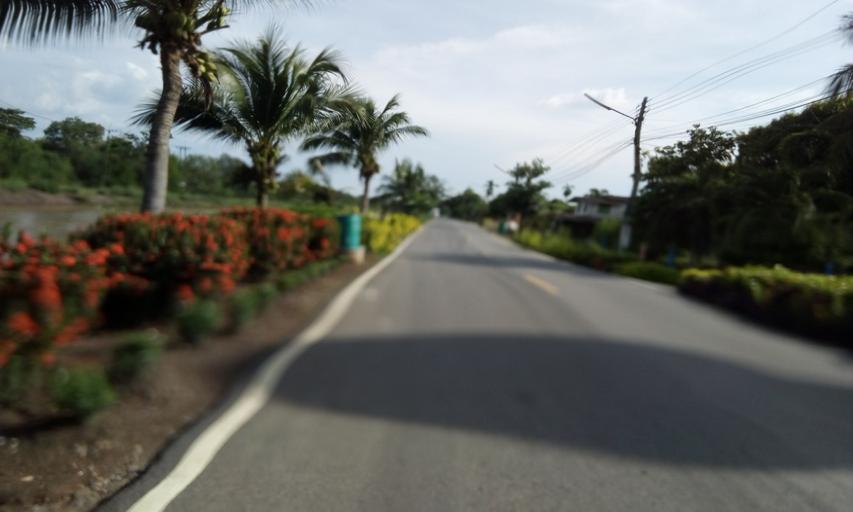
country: TH
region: Pathum Thani
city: Nong Suea
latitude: 14.1649
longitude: 100.8232
